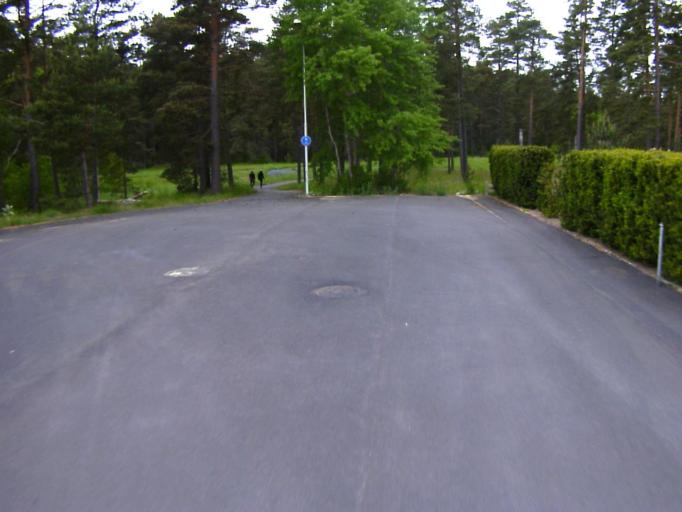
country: SE
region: Skane
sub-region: Kristianstads Kommun
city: Ahus
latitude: 55.9439
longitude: 14.2894
